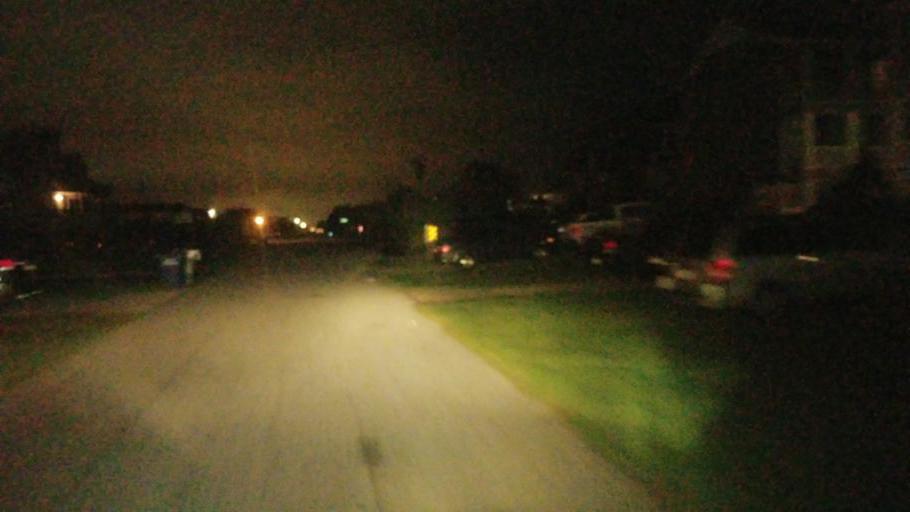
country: US
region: North Carolina
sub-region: Dare County
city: Nags Head
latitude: 35.9854
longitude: -75.6416
